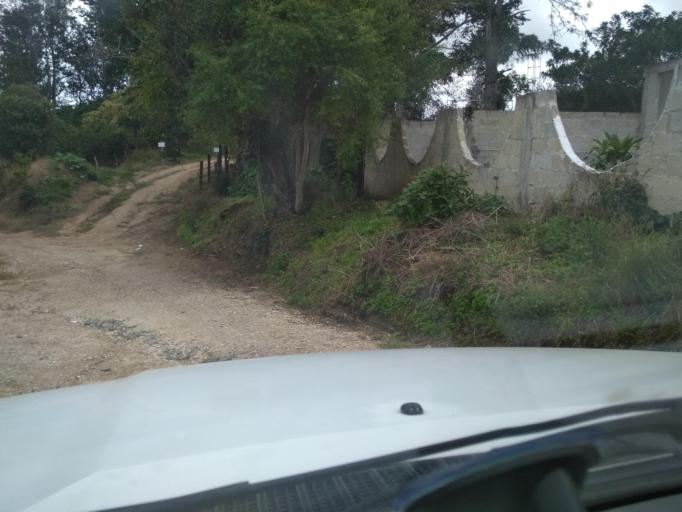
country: MX
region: Veracruz
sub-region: Emiliano Zapata
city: Dos Rios
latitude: 19.5368
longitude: -96.7943
